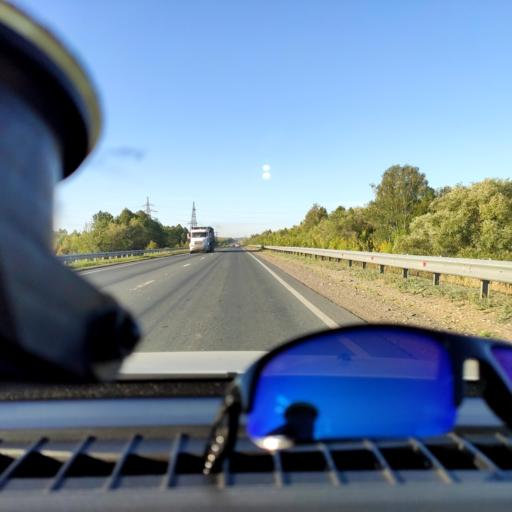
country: RU
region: Samara
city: Chapayevsk
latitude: 52.9847
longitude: 49.7623
